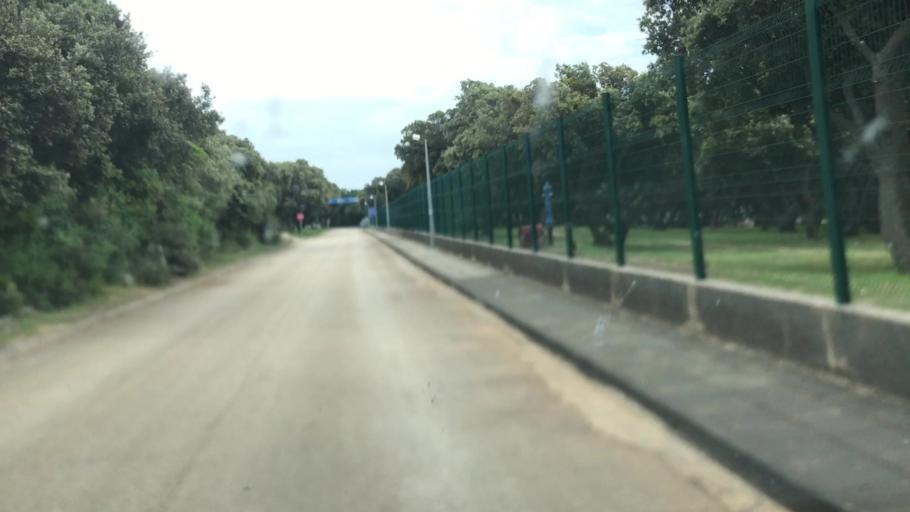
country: HR
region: Licko-Senjska
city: Novalja
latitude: 44.5406
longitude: 14.8853
